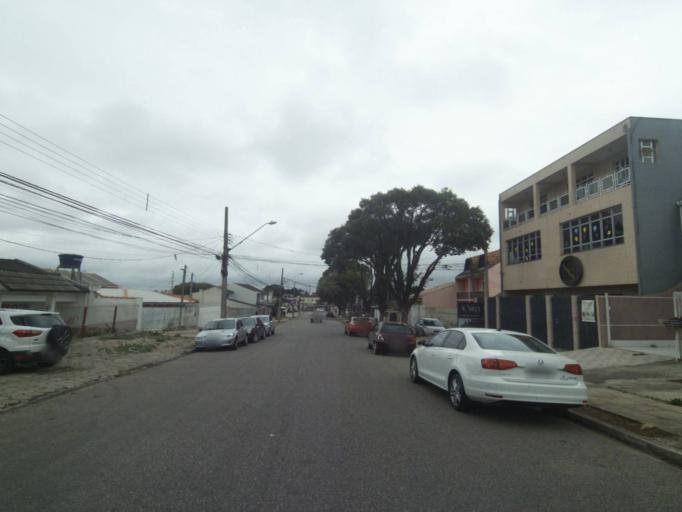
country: BR
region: Parana
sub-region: Sao Jose Dos Pinhais
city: Sao Jose dos Pinhais
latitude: -25.5422
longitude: -49.2790
